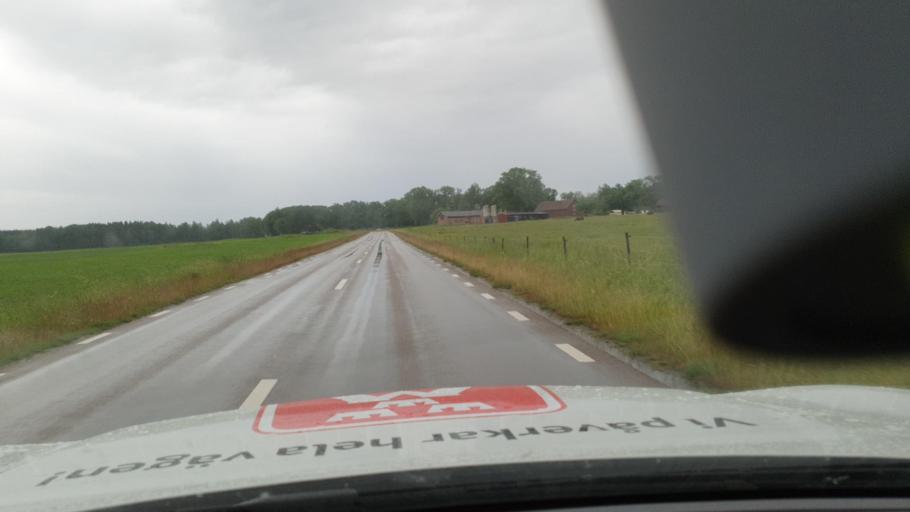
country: SE
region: Vaestra Goetaland
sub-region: Mariestads Kommun
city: Mariestad
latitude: 58.7510
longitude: 13.9070
